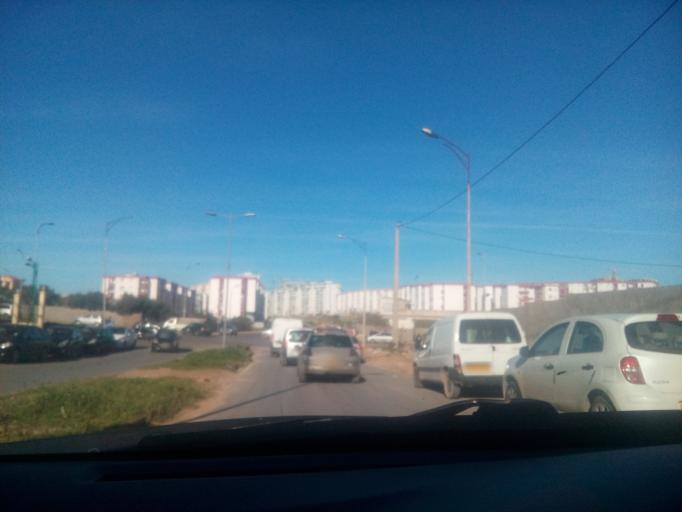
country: DZ
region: Oran
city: Bir el Djir
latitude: 35.7501
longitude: -0.5519
